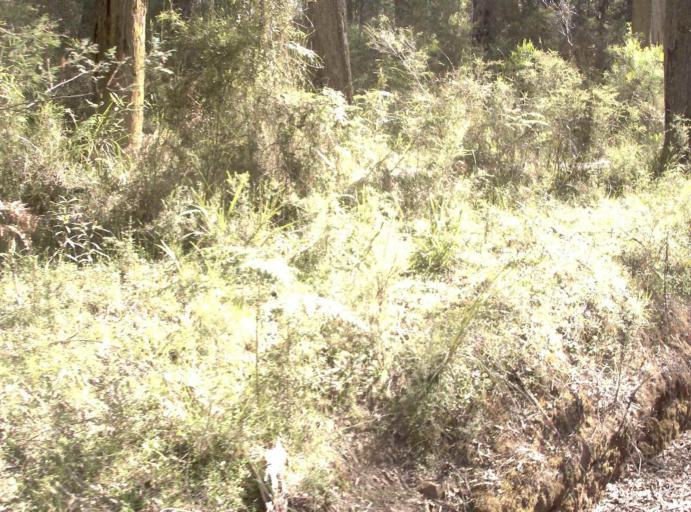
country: AU
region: New South Wales
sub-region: Bombala
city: Bombala
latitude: -37.3780
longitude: 148.6798
